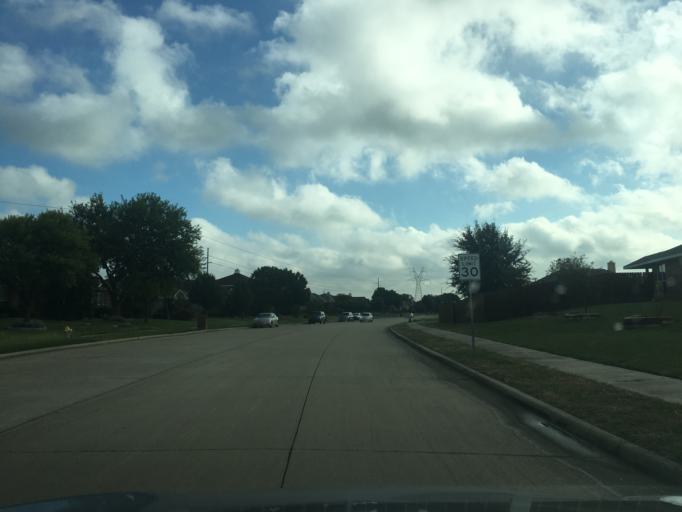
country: US
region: Texas
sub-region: Dallas County
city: Sachse
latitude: 32.9638
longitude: -96.5896
